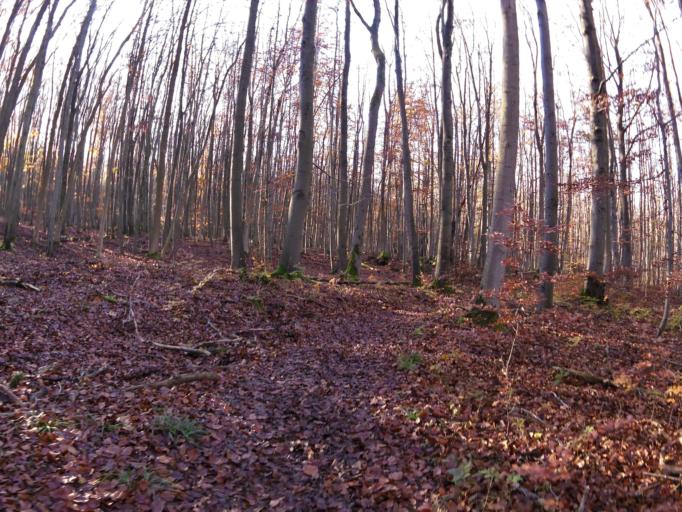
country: DE
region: Thuringia
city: Kammerforst
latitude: 51.0633
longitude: 10.4469
